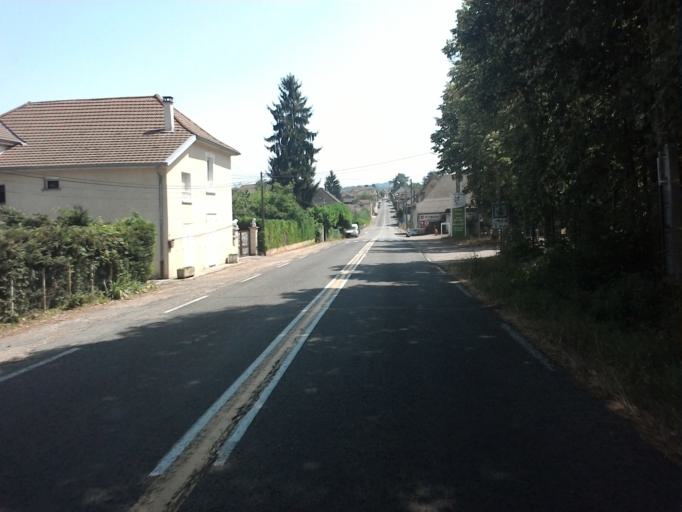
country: FR
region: Rhone-Alpes
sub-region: Departement de l'Isere
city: Les Abrets
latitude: 45.5423
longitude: 5.5814
